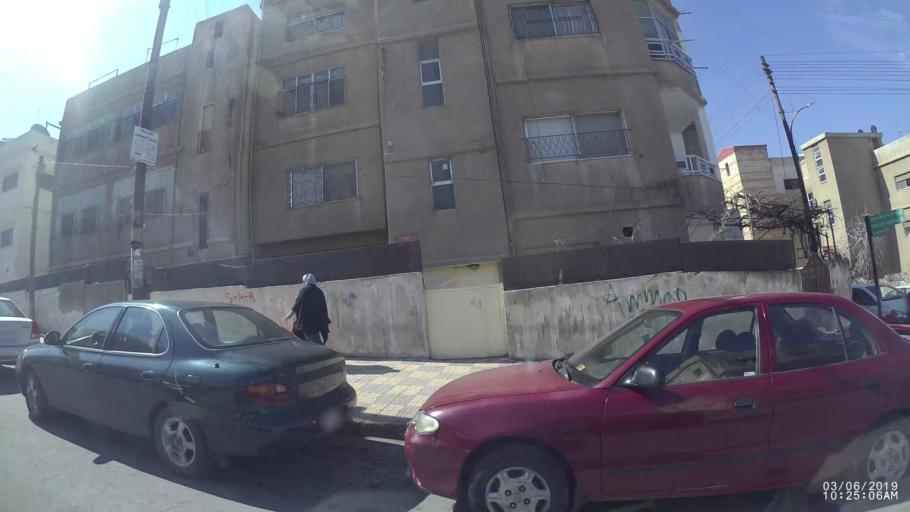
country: JO
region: Amman
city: Amman
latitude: 31.9805
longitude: 35.9844
